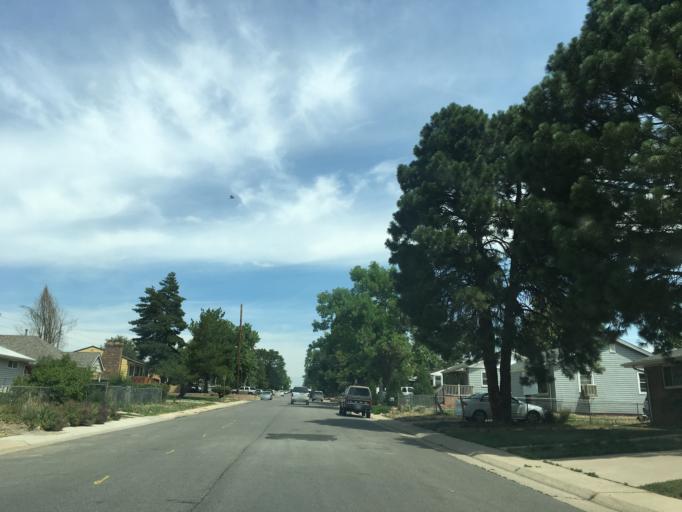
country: US
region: Colorado
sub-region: Jefferson County
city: Lakewood
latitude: 39.6941
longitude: -105.0414
